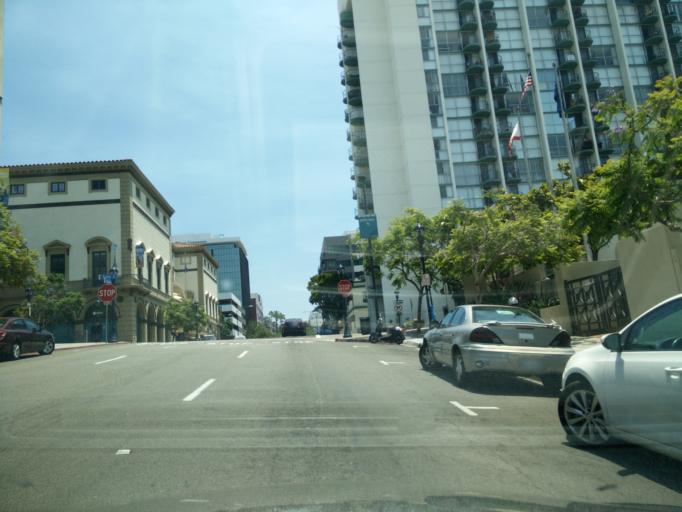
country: US
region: California
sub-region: San Diego County
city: San Diego
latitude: 32.7219
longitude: -117.1625
